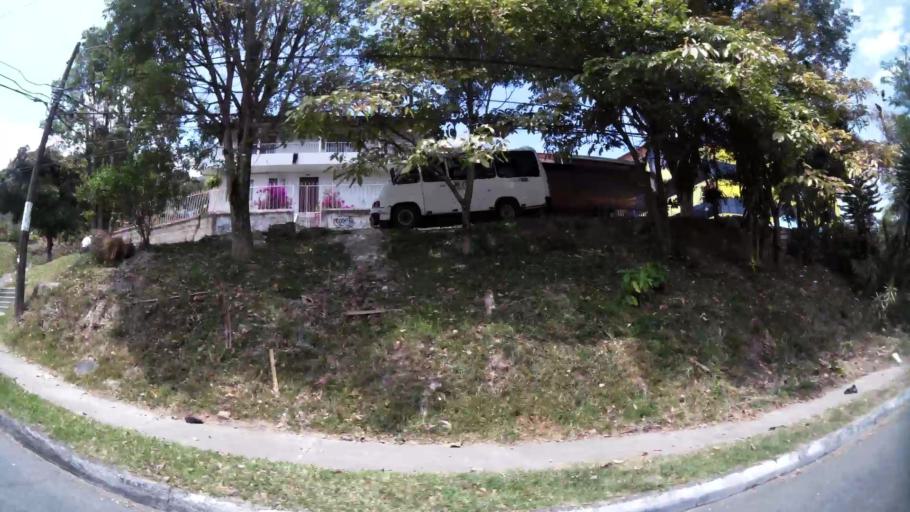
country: CO
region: Antioquia
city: Bello
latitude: 6.2987
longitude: -75.5810
